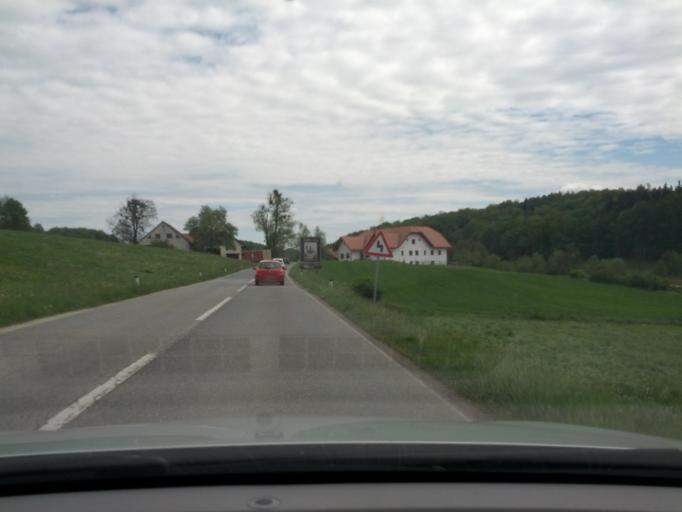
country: SI
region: Smarje pri Jelsah
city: Smarje pri Jelsah
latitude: 46.2321
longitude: 15.5408
